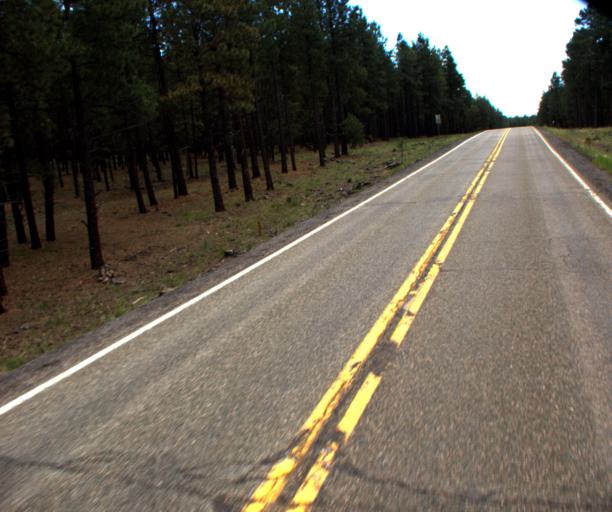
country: US
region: Arizona
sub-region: Coconino County
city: Parks
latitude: 35.3481
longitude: -111.7898
